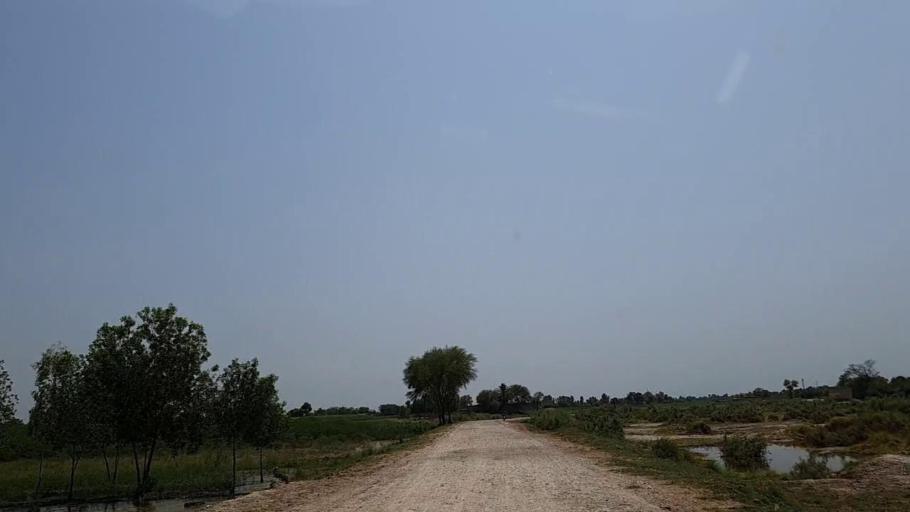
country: PK
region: Sindh
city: Adilpur
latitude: 27.9725
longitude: 69.3978
